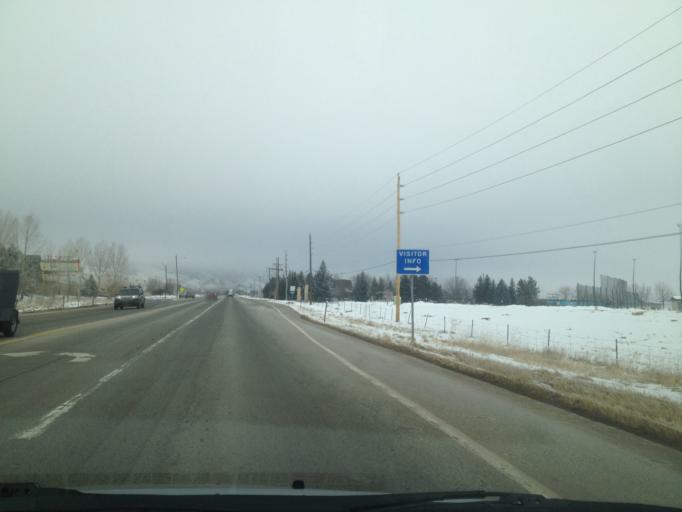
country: US
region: Colorado
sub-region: Boulder County
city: Boulder
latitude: 40.0610
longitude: -105.2750
